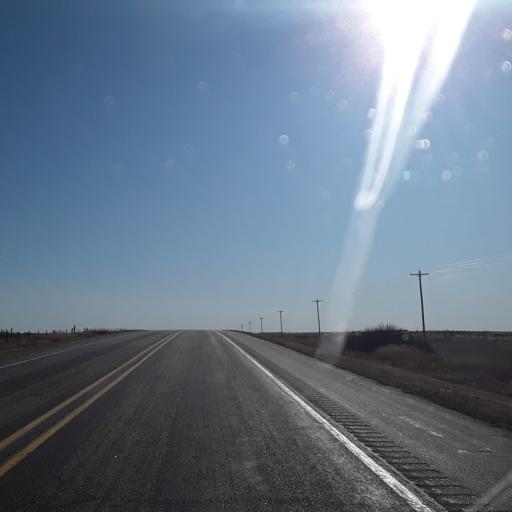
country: US
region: Nebraska
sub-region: Frontier County
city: Stockville
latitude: 40.5772
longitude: -100.6298
